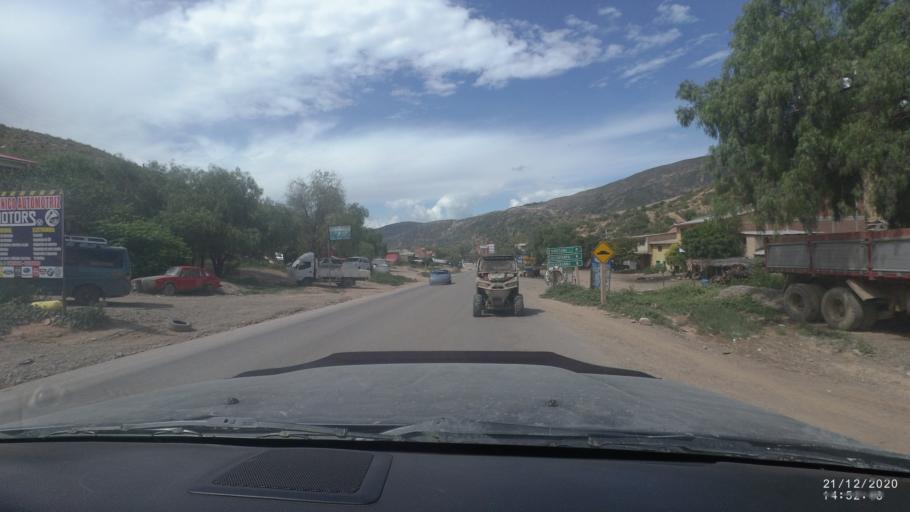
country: BO
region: Cochabamba
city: Sipe Sipe
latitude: -17.5635
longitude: -66.3480
